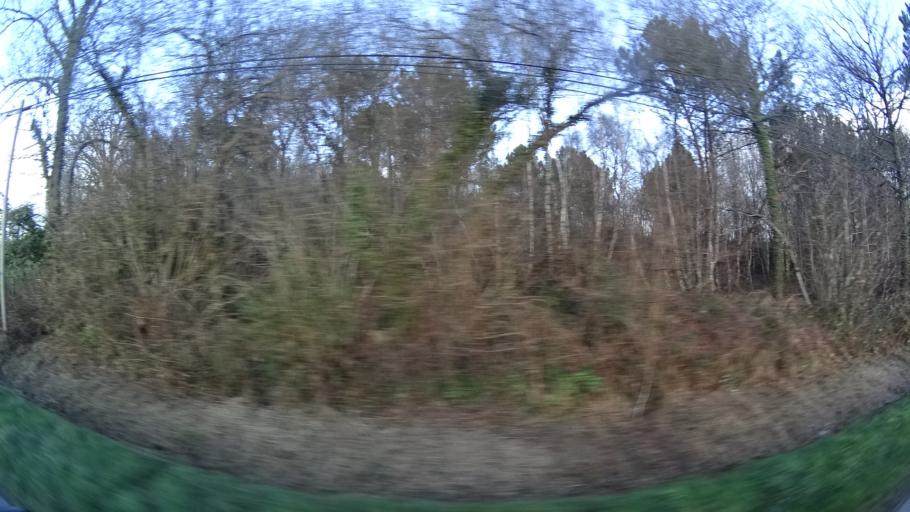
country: FR
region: Pays de la Loire
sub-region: Departement de la Loire-Atlantique
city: Fegreac
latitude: 47.5826
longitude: -1.9954
